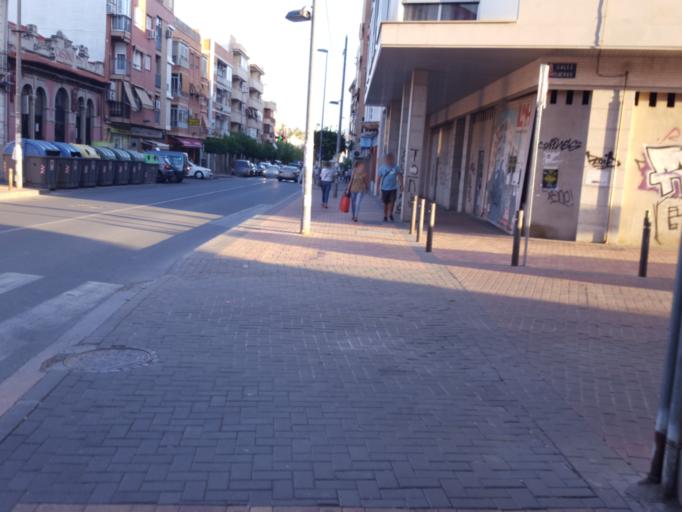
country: ES
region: Murcia
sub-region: Murcia
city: Murcia
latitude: 38.0099
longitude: -1.1534
